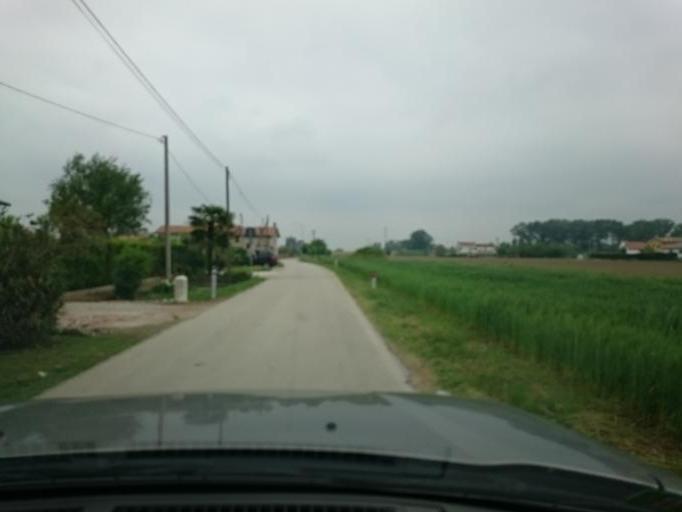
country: IT
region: Veneto
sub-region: Provincia di Padova
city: Cartura
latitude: 45.2924
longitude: 11.8583
